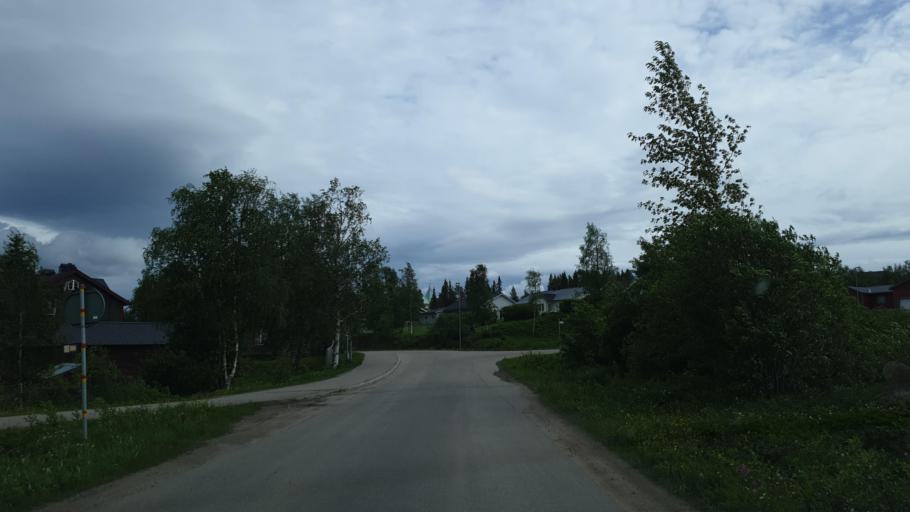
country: SE
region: Norrbotten
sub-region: Gallivare Kommun
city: Gaellivare
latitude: 67.1279
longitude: 20.6520
